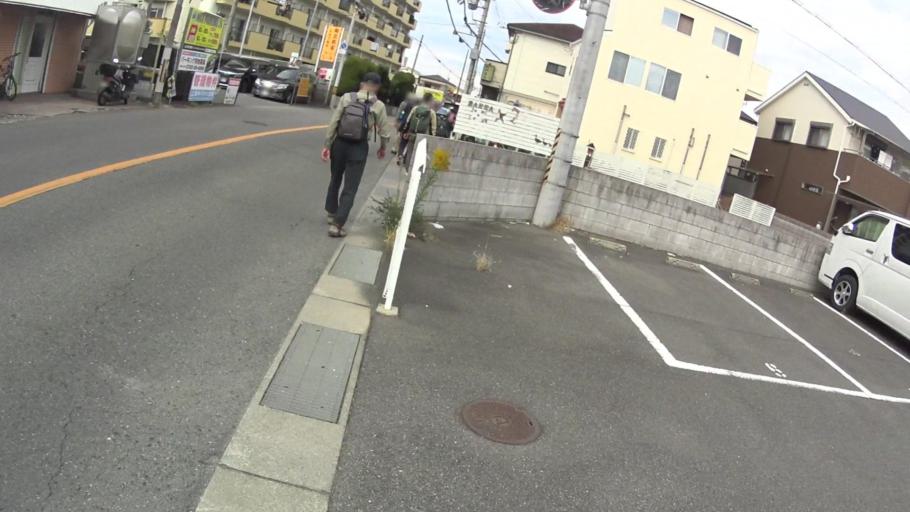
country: JP
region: Osaka
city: Kashihara
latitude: 34.5603
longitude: 135.5923
